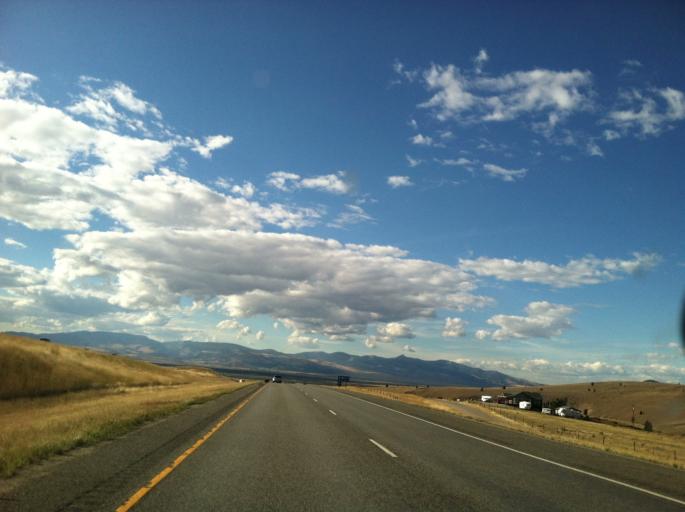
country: US
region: Montana
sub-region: Deer Lodge County
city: Warm Springs
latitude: 46.0433
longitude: -112.7411
